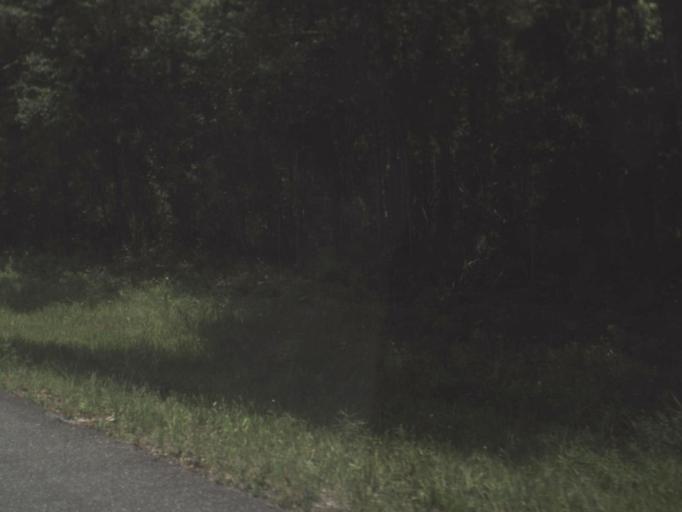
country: US
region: Florida
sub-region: Lafayette County
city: Mayo
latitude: 29.9176
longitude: -83.2872
